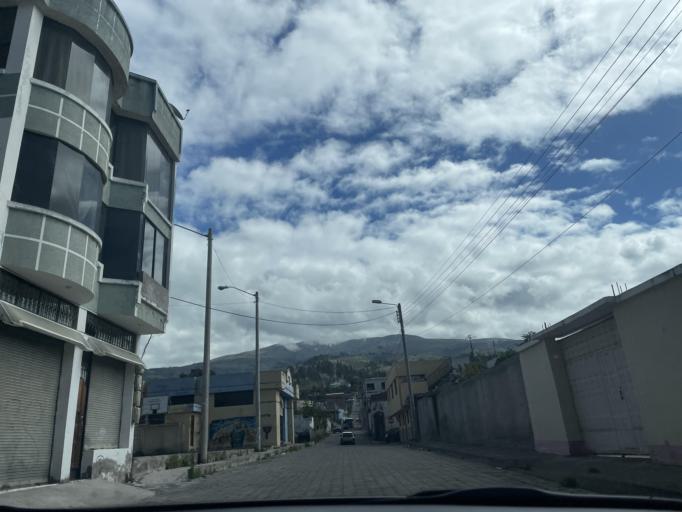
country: EC
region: Chimborazo
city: Guano
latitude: -1.6081
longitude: -78.6405
